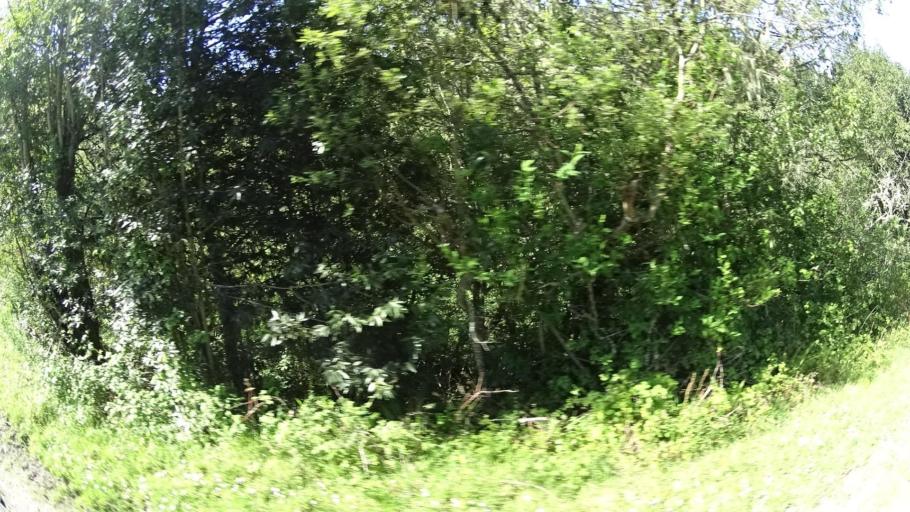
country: US
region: California
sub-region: Humboldt County
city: Fortuna
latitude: 40.5290
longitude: -124.1772
